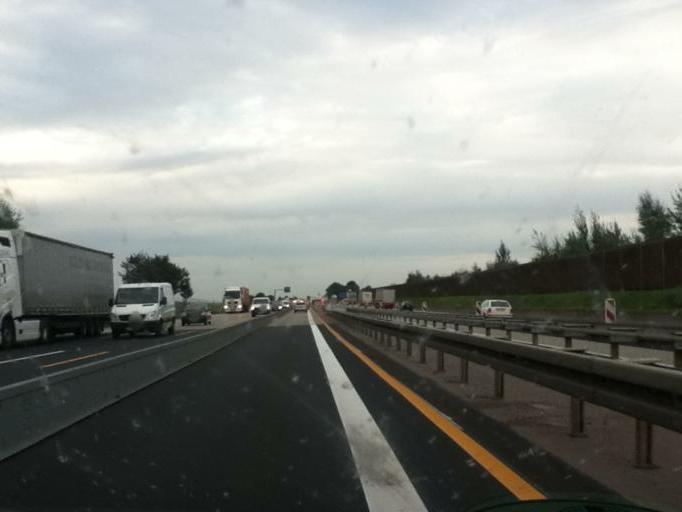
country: DE
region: Saxony
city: Wilsdruff
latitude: 51.0609
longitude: 13.5337
